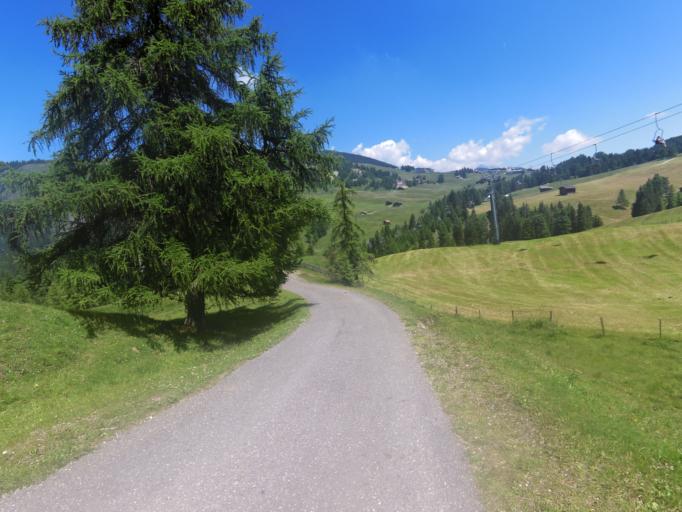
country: IT
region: Trentino-Alto Adige
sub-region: Bolzano
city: Siusi
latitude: 46.5353
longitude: 11.6034
